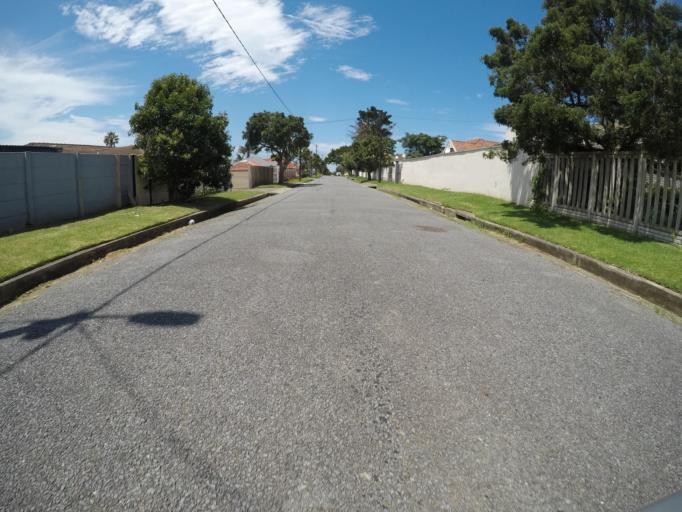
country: ZA
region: Eastern Cape
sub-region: Buffalo City Metropolitan Municipality
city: East London
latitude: -33.0334
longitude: 27.8575
